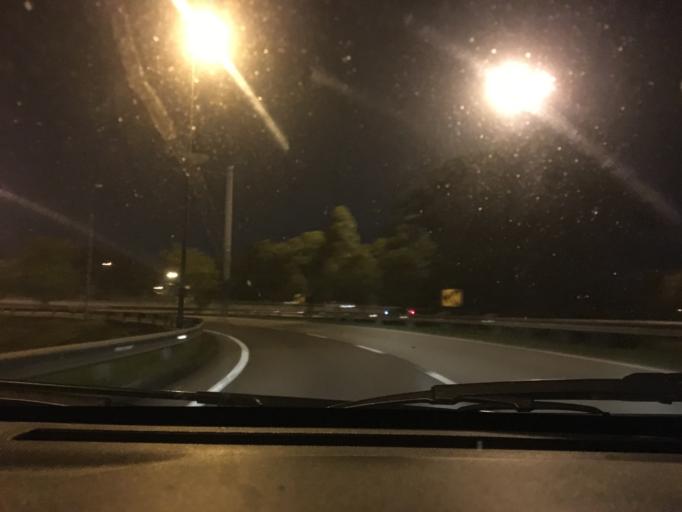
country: MY
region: Selangor
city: Kampong Baharu Balakong
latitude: 2.9797
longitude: 101.7342
